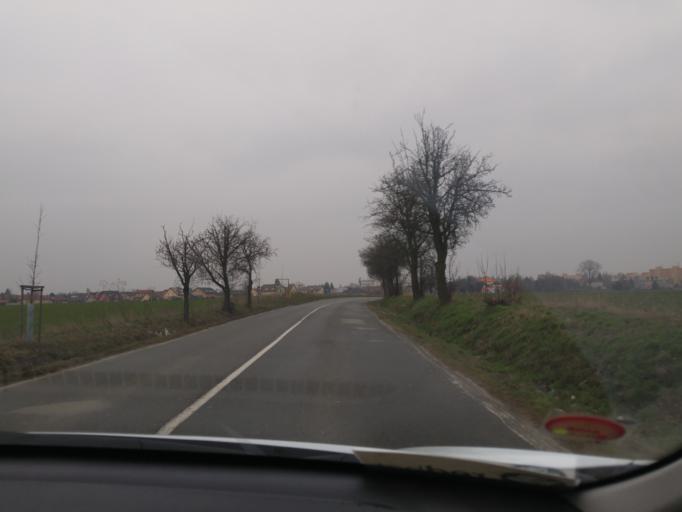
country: CZ
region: Central Bohemia
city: Brandys nad Labem-Stara Boleslav
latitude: 50.1941
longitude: 14.6414
